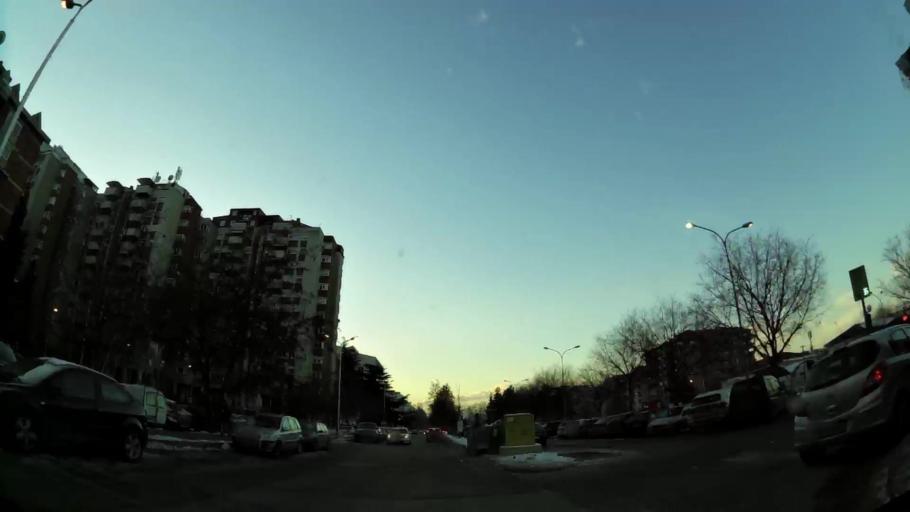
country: MK
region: Karpos
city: Skopje
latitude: 41.9947
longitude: 21.4129
